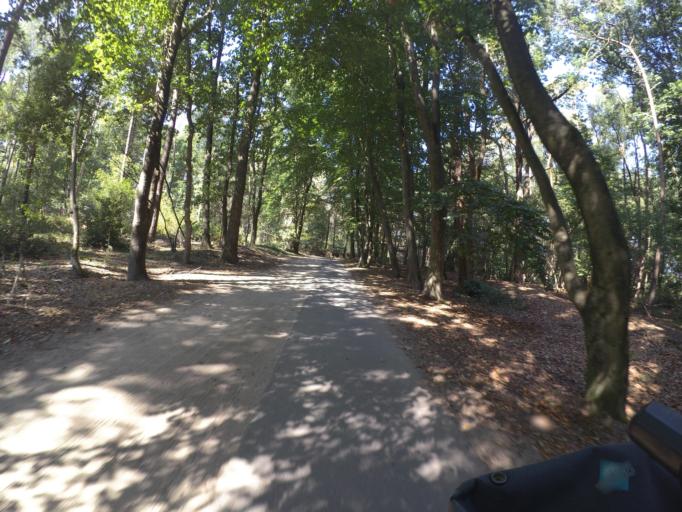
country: NL
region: Overijssel
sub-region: Gemeente Twenterand
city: Den Ham
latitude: 52.3838
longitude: 6.4421
